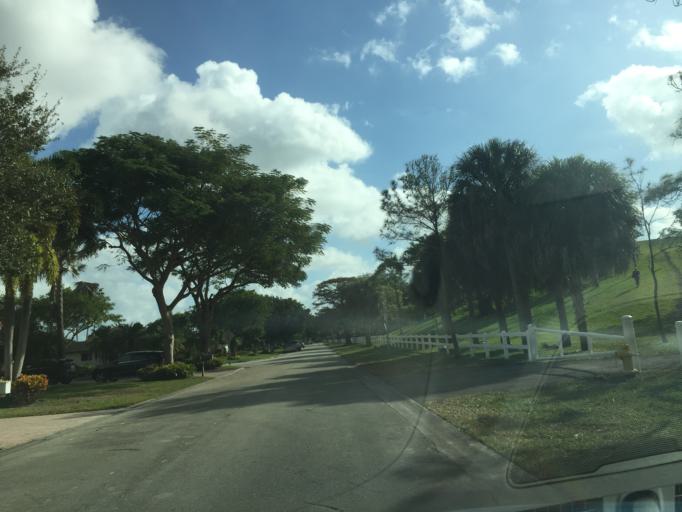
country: US
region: Florida
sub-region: Broward County
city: Tamarac
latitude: 26.2322
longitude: -80.2486
